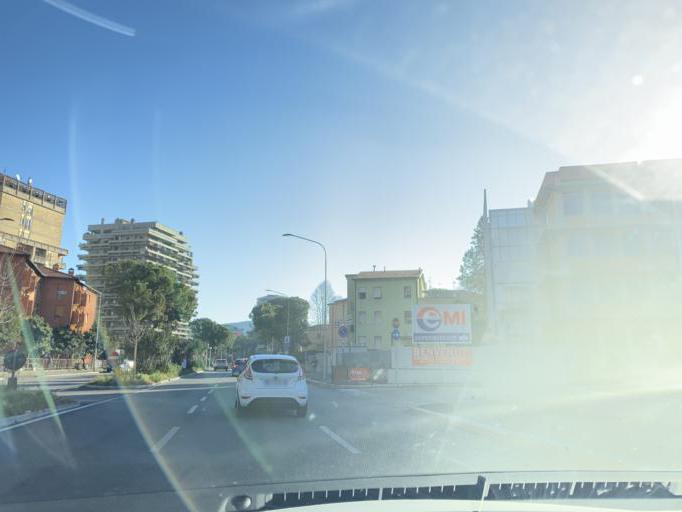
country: IT
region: Umbria
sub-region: Provincia di Terni
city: Terni
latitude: 42.5526
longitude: 12.6427
